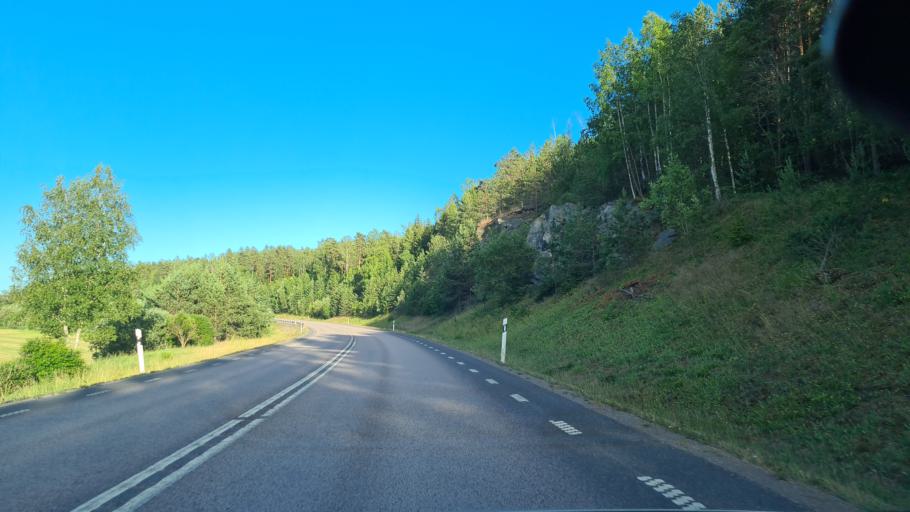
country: SE
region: Soedermanland
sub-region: Gnesta Kommun
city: Gnesta
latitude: 59.0354
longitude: 17.3022
